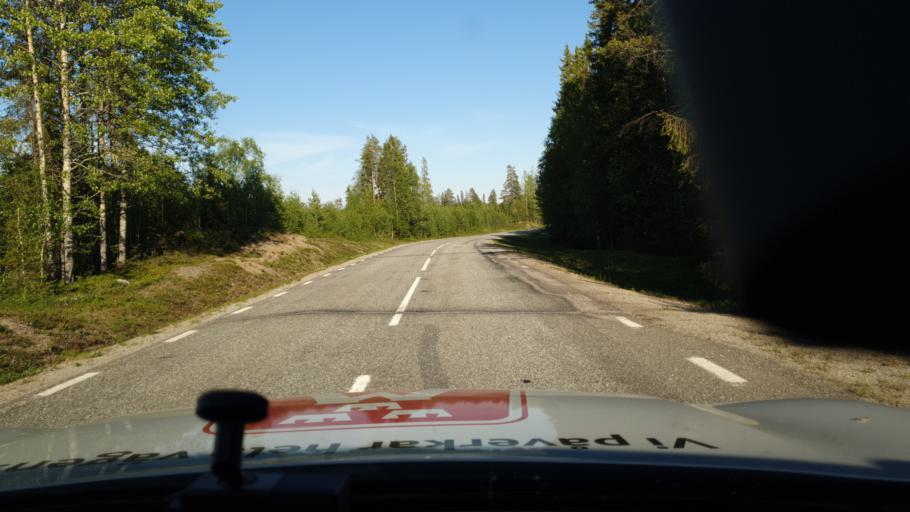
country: SE
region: Vaesterbotten
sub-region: Lycksele Kommun
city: Soderfors
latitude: 64.6317
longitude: 18.0320
